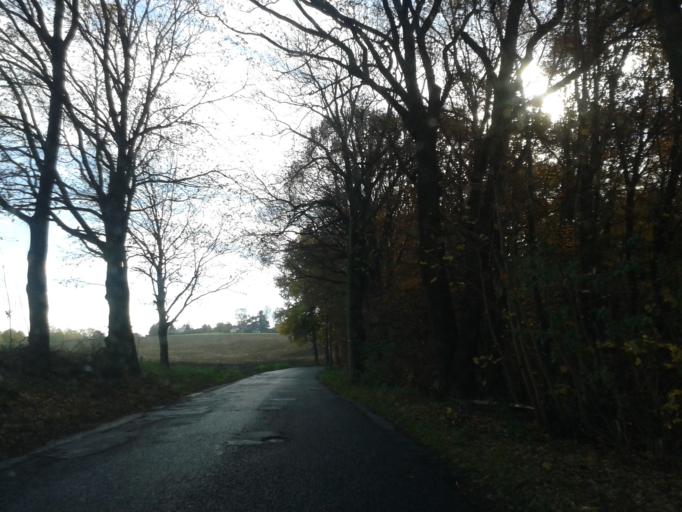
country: DE
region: Saxony
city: Albertstadt
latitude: 51.0547
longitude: 13.8365
